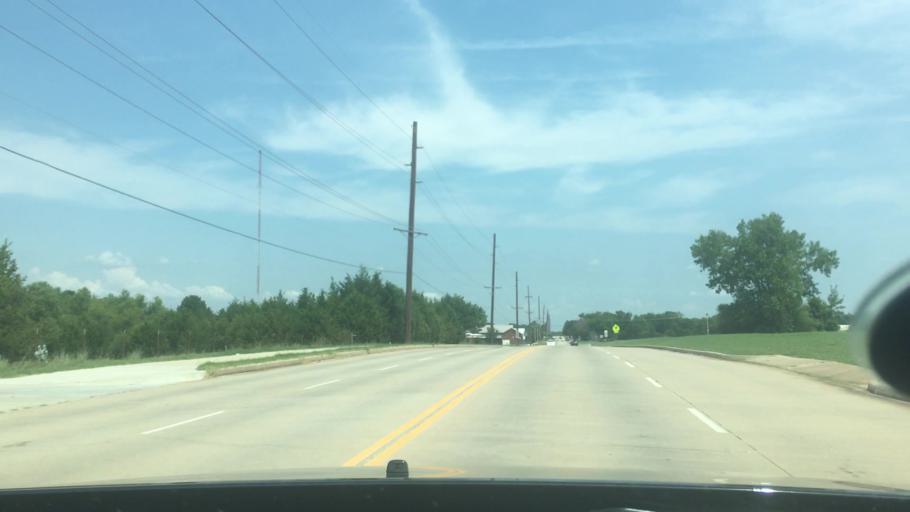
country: US
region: Oklahoma
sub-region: Pottawatomie County
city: Shawnee
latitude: 35.3586
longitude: -96.8943
